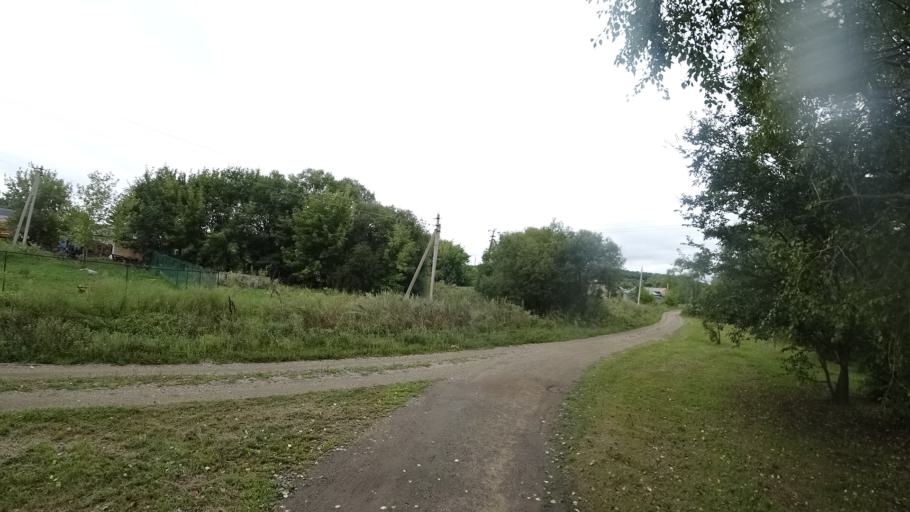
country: RU
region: Primorskiy
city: Chernigovka
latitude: 44.4584
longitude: 132.5941
